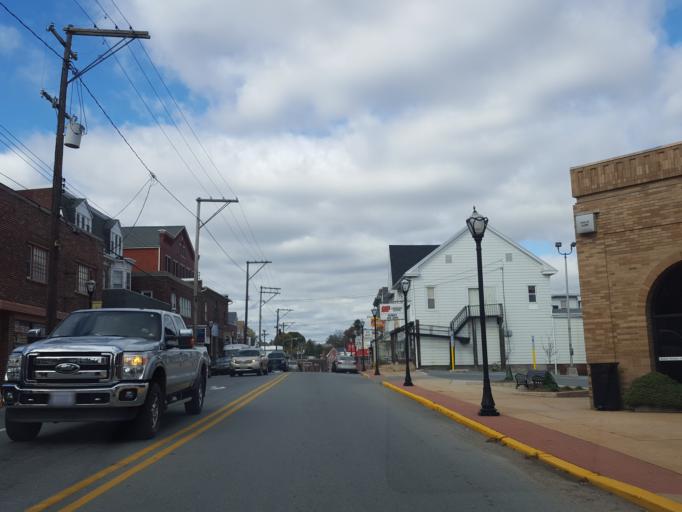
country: US
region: Pennsylvania
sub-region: York County
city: Red Lion
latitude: 39.9010
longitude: -76.6061
